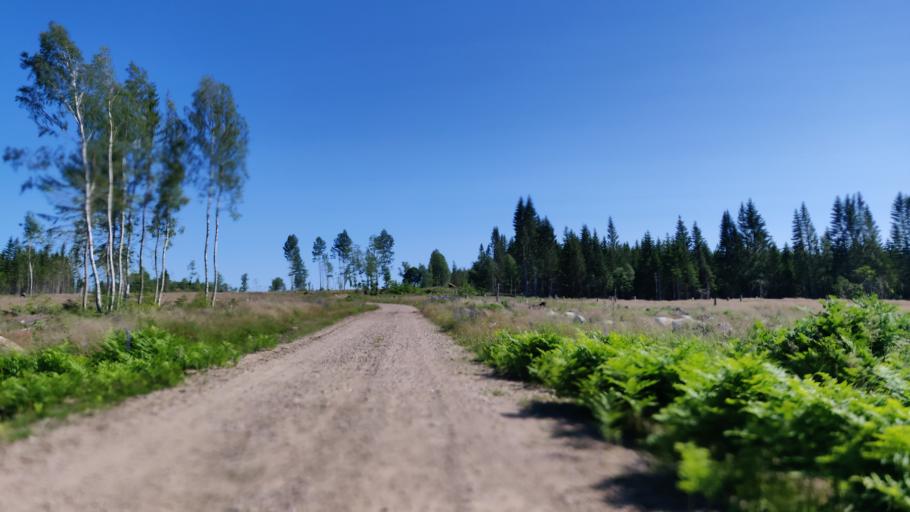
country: SE
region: Vaermland
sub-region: Hagfors Kommun
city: Hagfors
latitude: 59.9727
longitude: 13.6041
